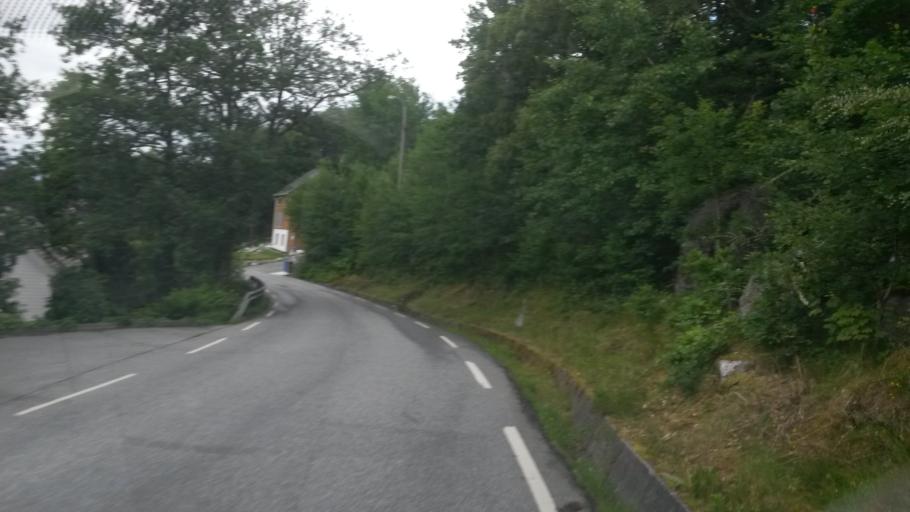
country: NO
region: Rogaland
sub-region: Sandnes
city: Sandnes
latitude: 58.8822
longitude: 5.7755
